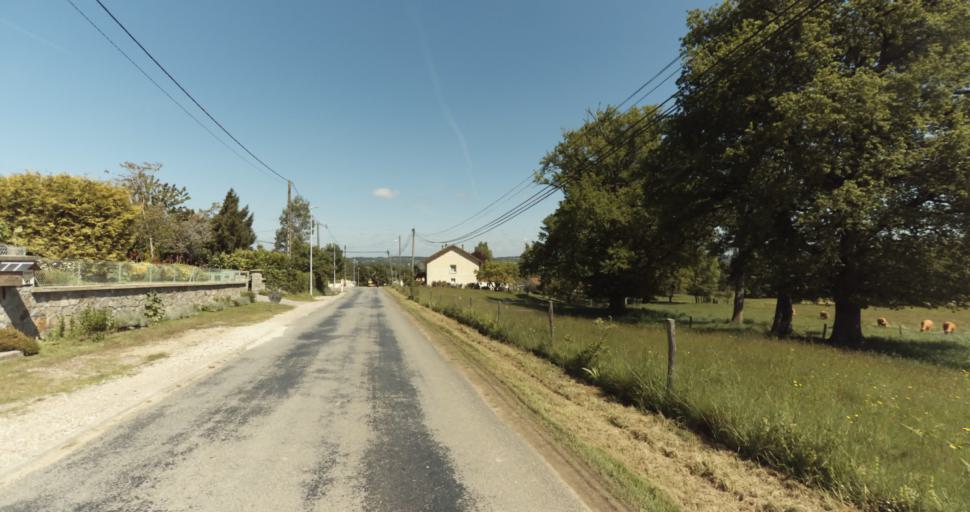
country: FR
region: Limousin
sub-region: Departement de la Haute-Vienne
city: Le Vigen
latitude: 45.7360
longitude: 1.2881
